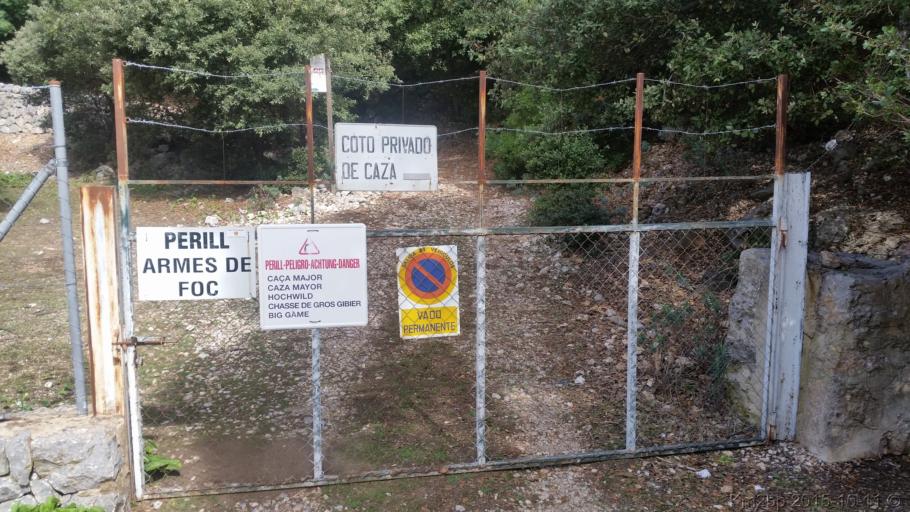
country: ES
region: Balearic Islands
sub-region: Illes Balears
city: Fornalutx
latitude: 39.7927
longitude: 2.7323
